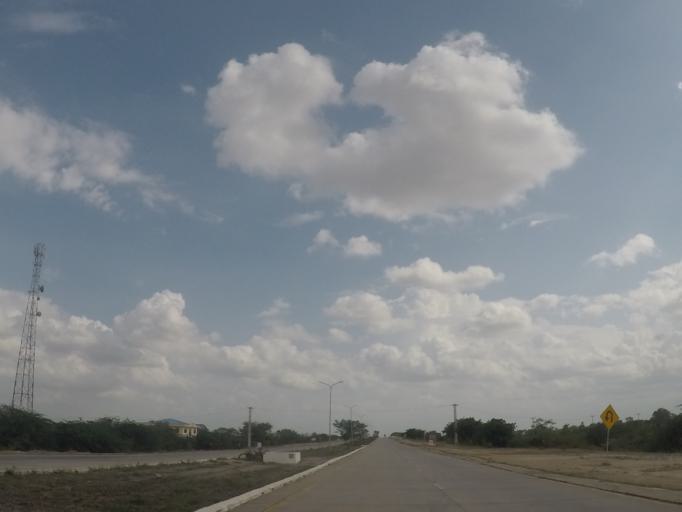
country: MM
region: Mandalay
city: Kyaukse
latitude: 21.3988
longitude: 95.8956
